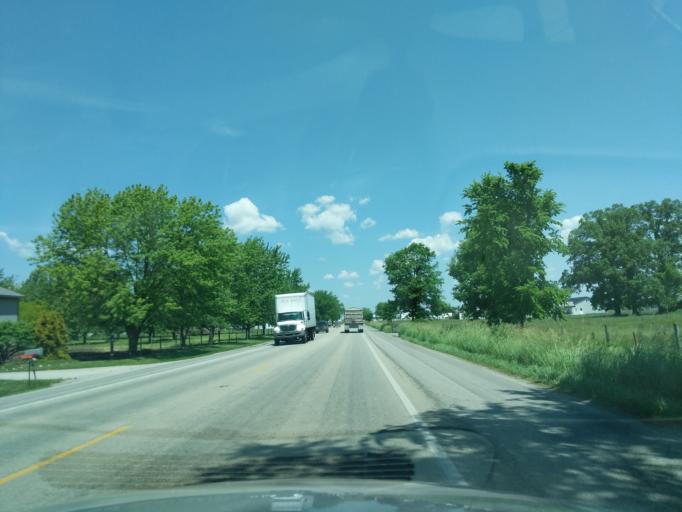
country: US
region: Indiana
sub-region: LaGrange County
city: Topeka
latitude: 41.5704
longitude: -85.5785
